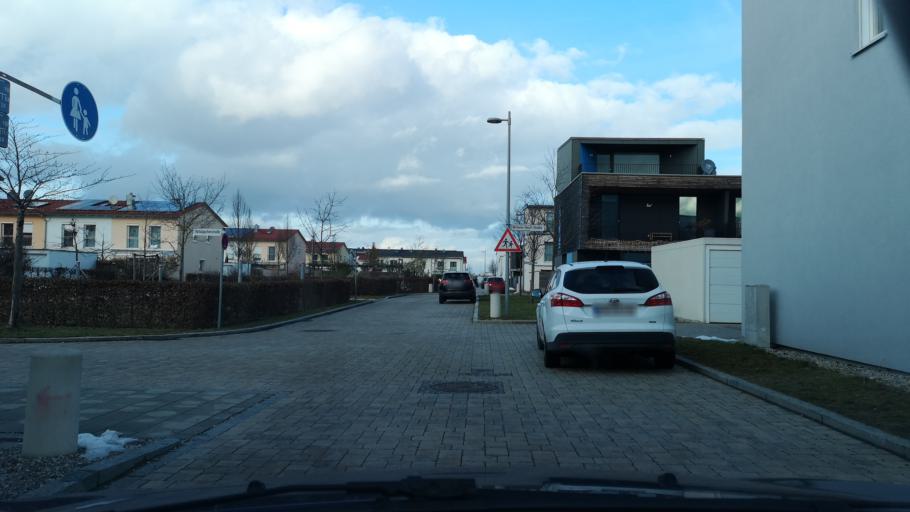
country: DE
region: Bavaria
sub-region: Upper Bavaria
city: Pliening
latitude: 48.1787
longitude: 11.8024
